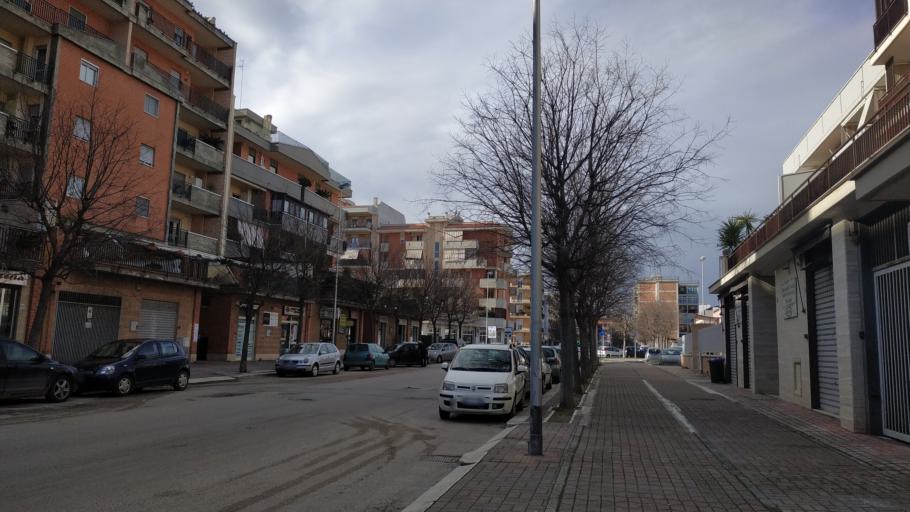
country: IT
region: Apulia
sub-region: Provincia di Barletta - Andria - Trani
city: Andria
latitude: 41.2368
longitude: 16.3025
